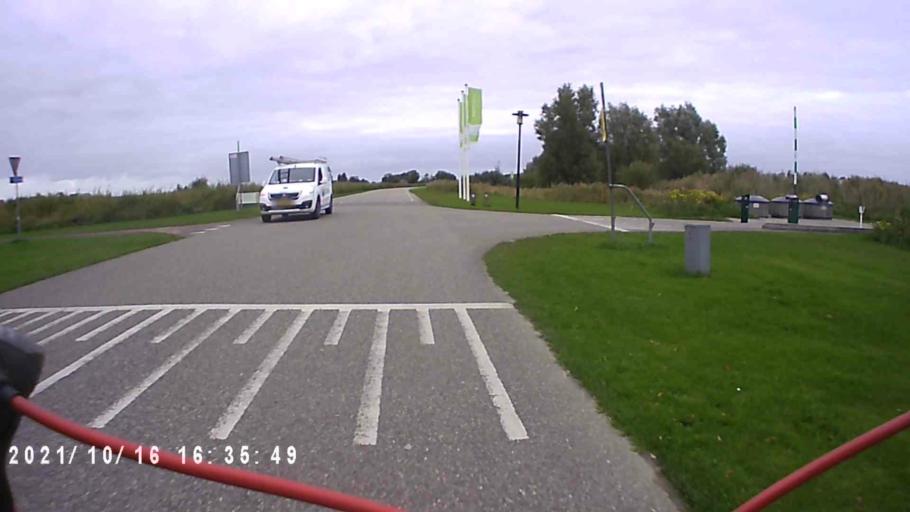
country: NL
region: Friesland
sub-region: Gemeente Dongeradeel
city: Anjum
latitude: 53.3761
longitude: 6.1531
